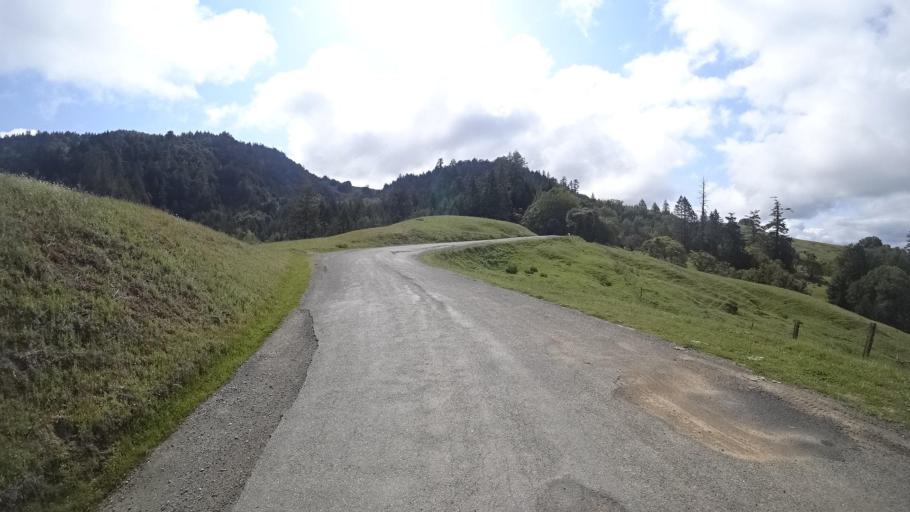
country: US
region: California
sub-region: Humboldt County
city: Redway
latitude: 40.1609
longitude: -123.5636
